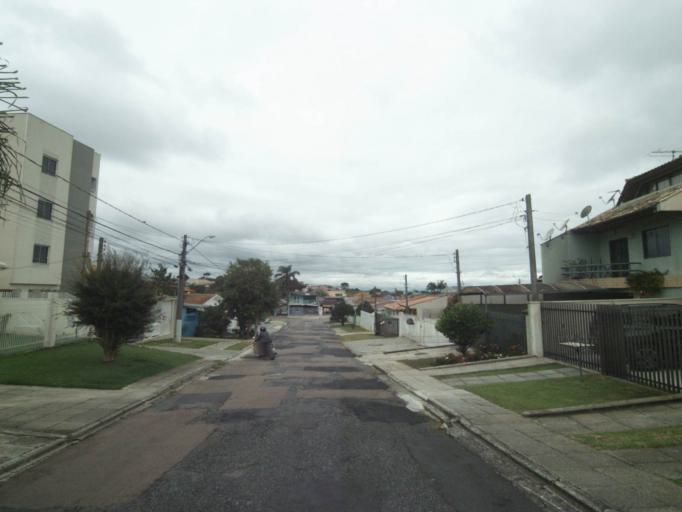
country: BR
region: Parana
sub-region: Curitiba
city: Curitiba
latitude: -25.4891
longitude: -49.2883
